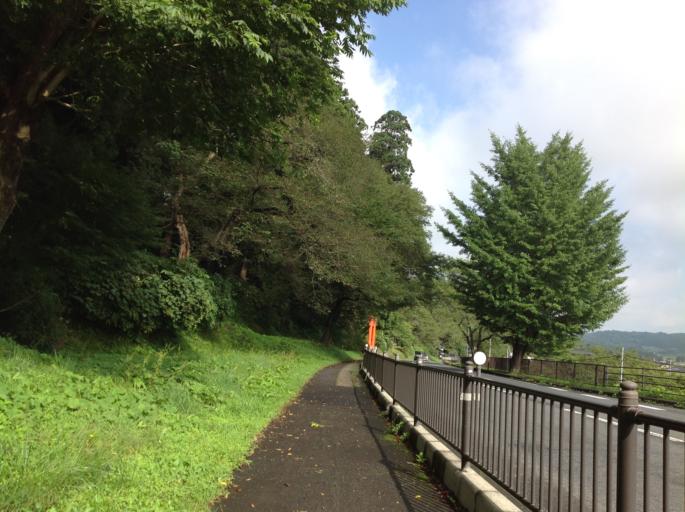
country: JP
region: Iwate
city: Ichinoseki
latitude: 38.9994
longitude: 141.1075
